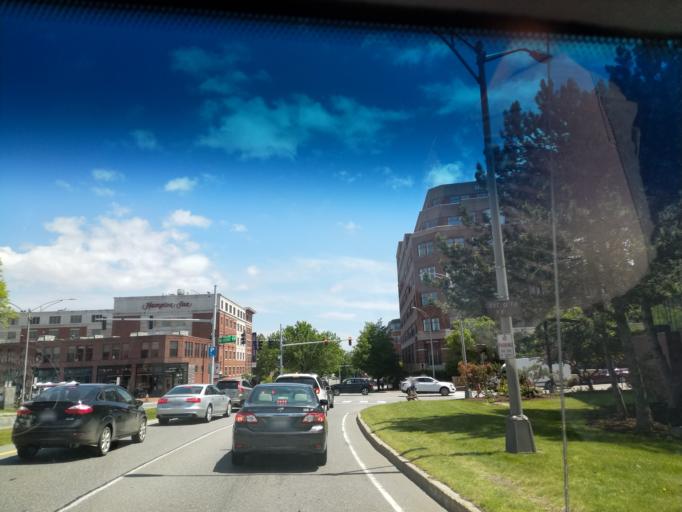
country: US
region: Maine
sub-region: Cumberland County
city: Portland
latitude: 43.6596
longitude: -70.2523
